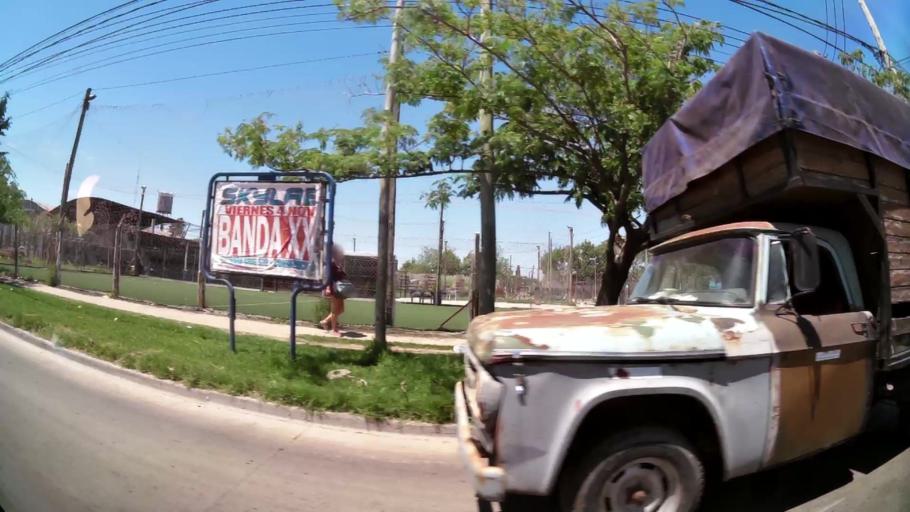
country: AR
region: Buenos Aires
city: Hurlingham
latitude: -34.5010
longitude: -58.7122
